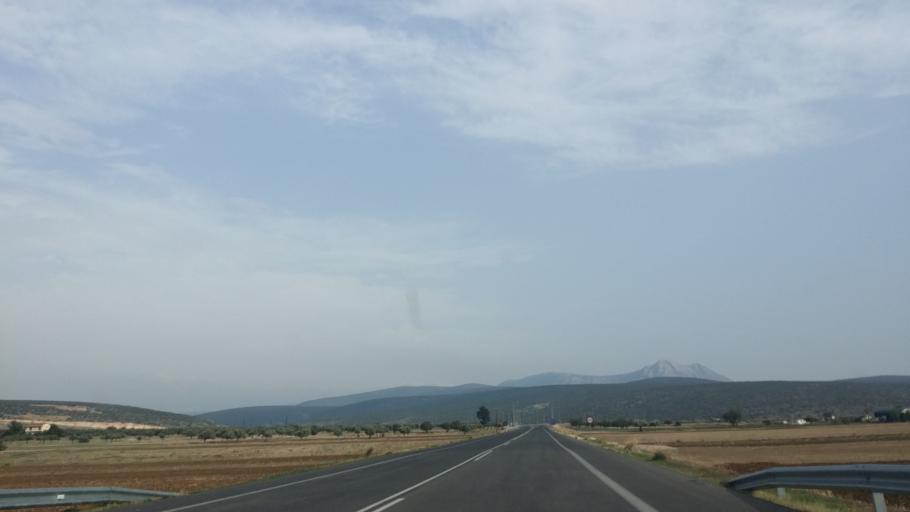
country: GR
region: Central Greece
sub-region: Nomos Voiotias
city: Korini
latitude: 38.2473
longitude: 22.9730
